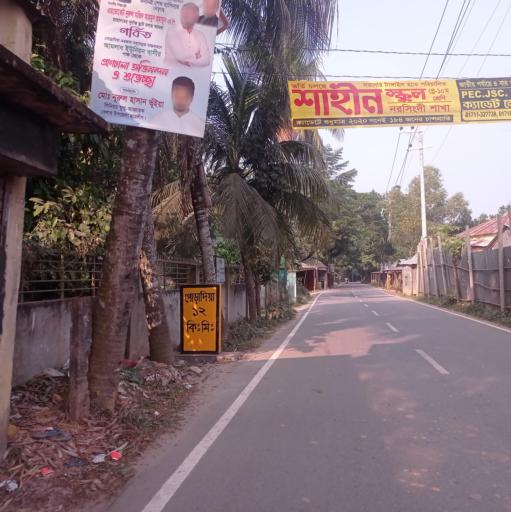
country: BD
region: Dhaka
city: Bhairab Bazar
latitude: 24.0834
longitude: 90.8494
